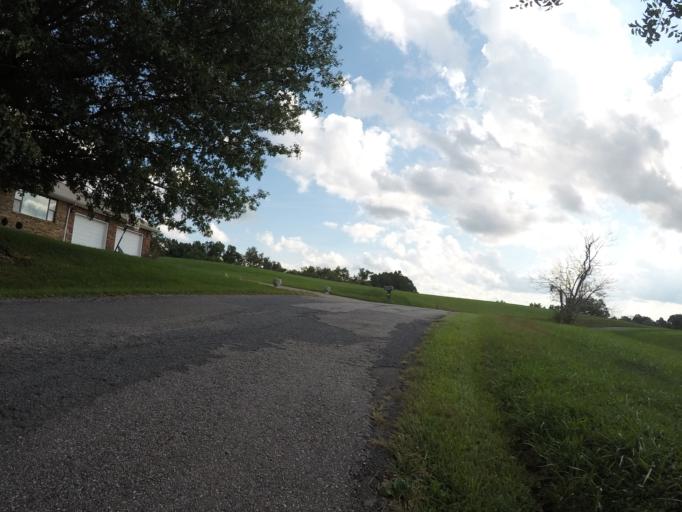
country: US
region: West Virginia
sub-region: Wayne County
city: Lavalette
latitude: 38.3614
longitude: -82.4638
